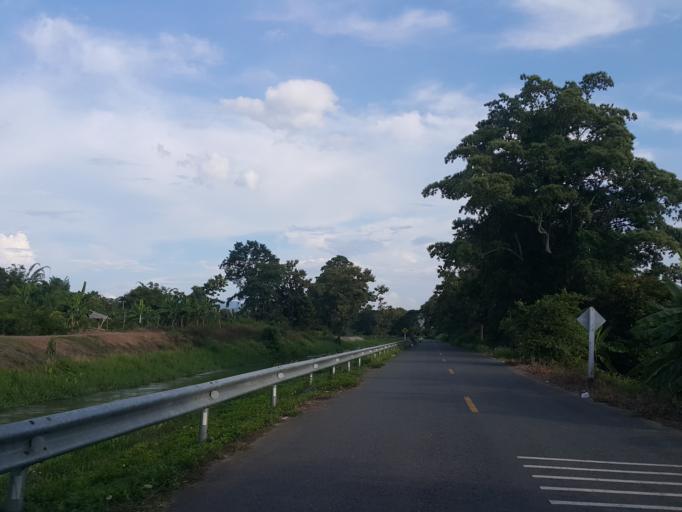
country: TH
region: Chiang Mai
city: Mae Taeng
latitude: 19.0655
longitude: 98.9621
